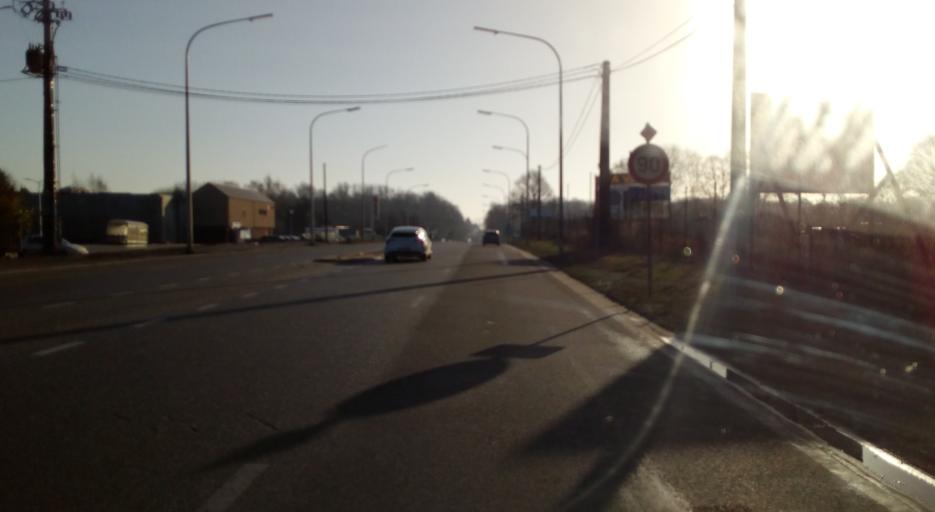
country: BE
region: Wallonia
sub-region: Province du Hainaut
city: Gerpinnes
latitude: 50.3292
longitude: 4.4759
